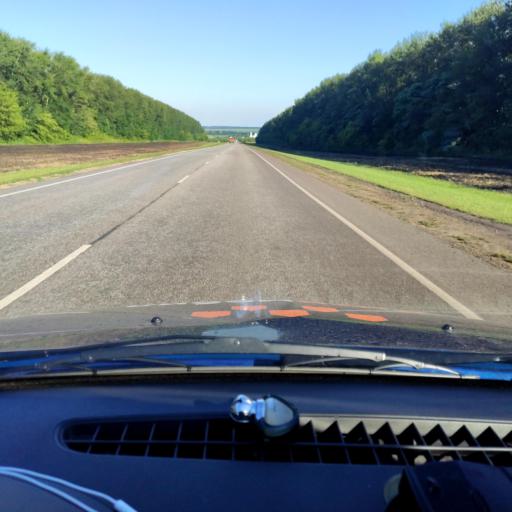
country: RU
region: Orjol
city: Zmiyevka
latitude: 52.6549
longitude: 36.5171
